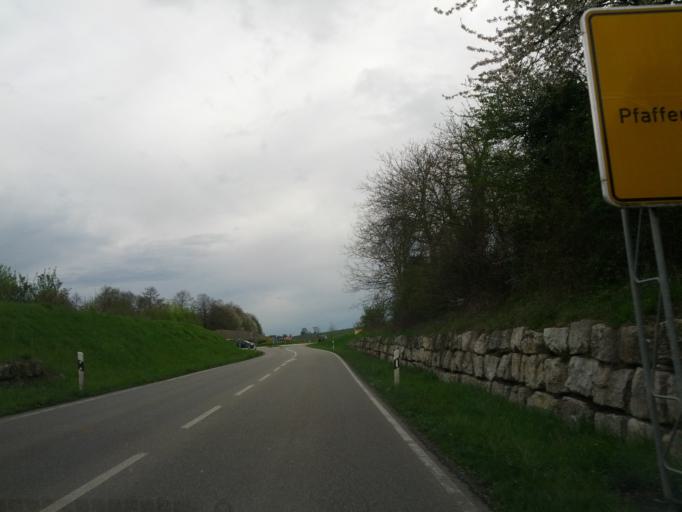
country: DE
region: Baden-Wuerttemberg
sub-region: Freiburg Region
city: Pfaffenweiler
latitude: 47.9389
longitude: 7.7510
